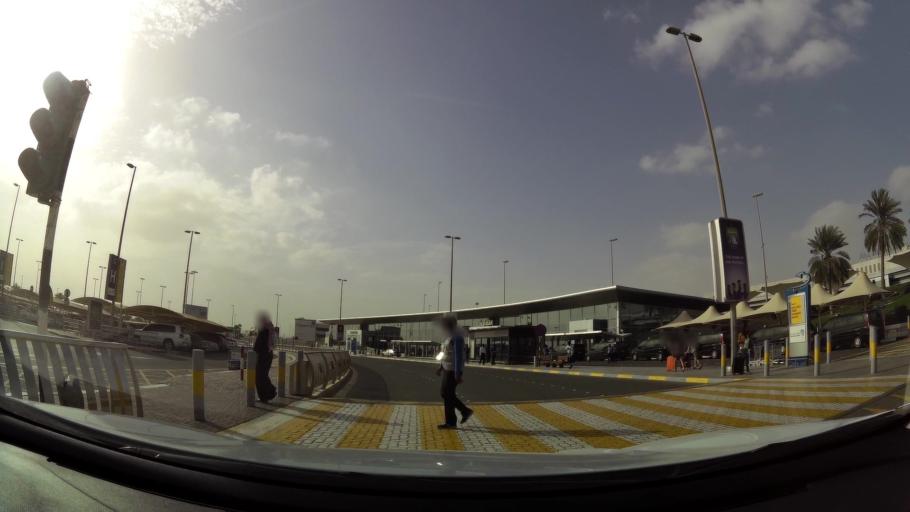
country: AE
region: Abu Dhabi
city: Abu Dhabi
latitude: 24.4264
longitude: 54.6456
